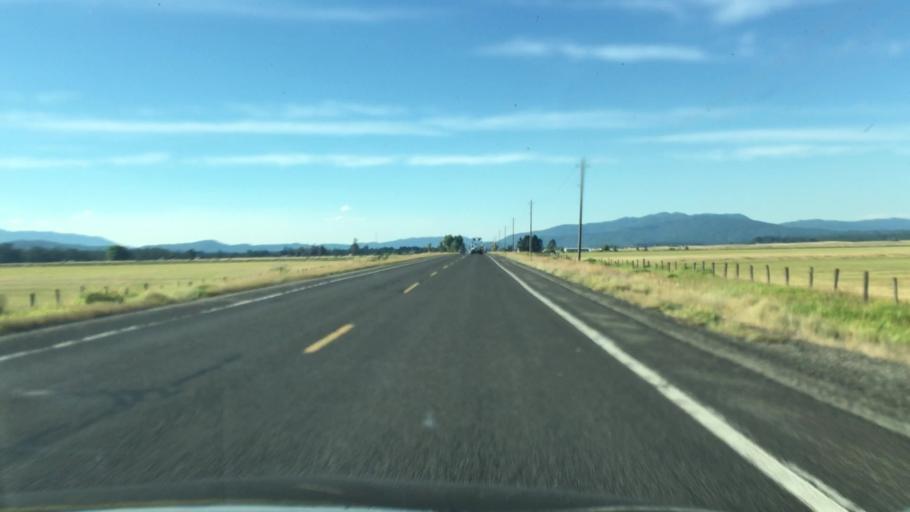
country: US
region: Idaho
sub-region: Valley County
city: Cascade
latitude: 44.4188
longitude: -115.9993
